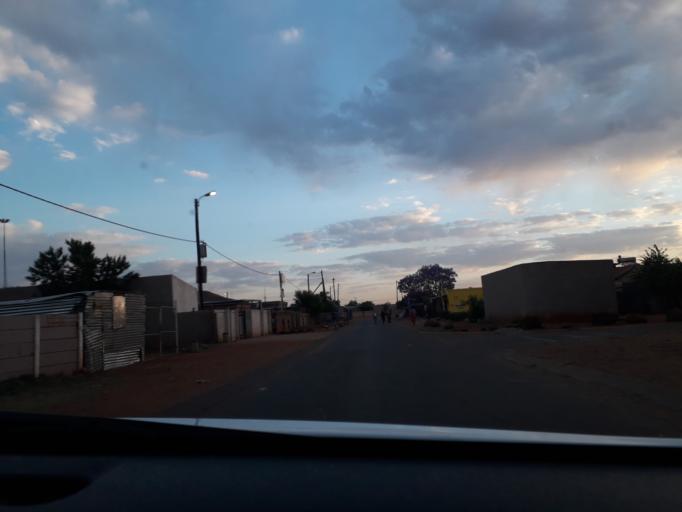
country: ZA
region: Gauteng
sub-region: Ekurhuleni Metropolitan Municipality
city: Germiston
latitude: -26.3115
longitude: 28.1998
